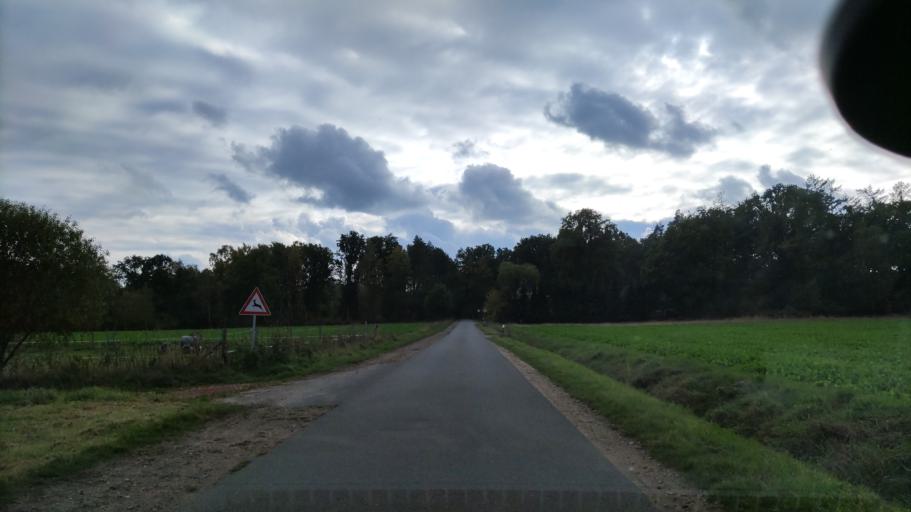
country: DE
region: Lower Saxony
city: Jelmstorf
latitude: 53.1389
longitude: 10.5306
